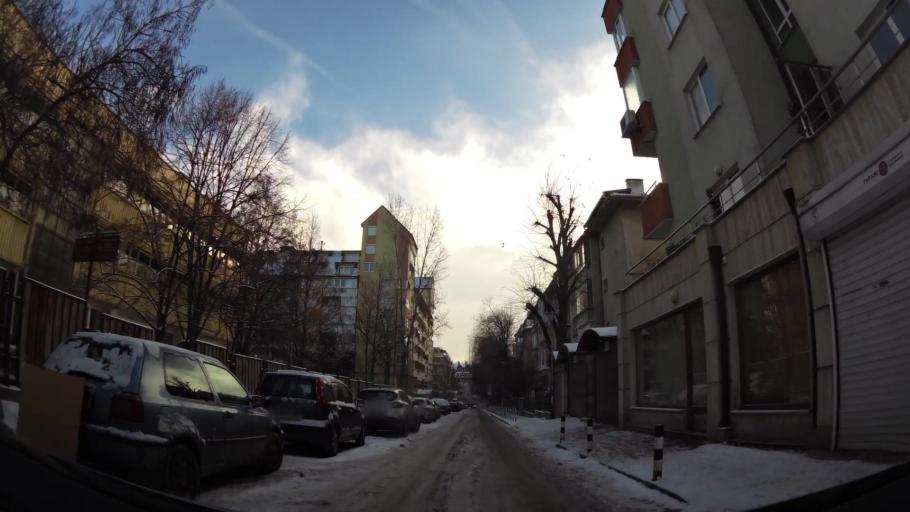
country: BG
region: Sofia-Capital
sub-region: Stolichna Obshtina
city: Sofia
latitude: 42.6724
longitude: 23.3311
